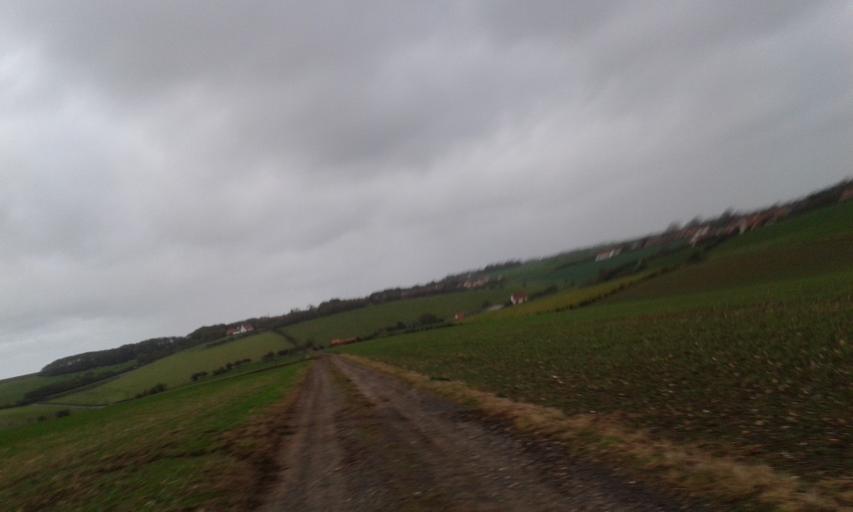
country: FR
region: Nord-Pas-de-Calais
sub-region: Departement du Pas-de-Calais
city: Ferques
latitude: 50.8690
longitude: 1.7270
